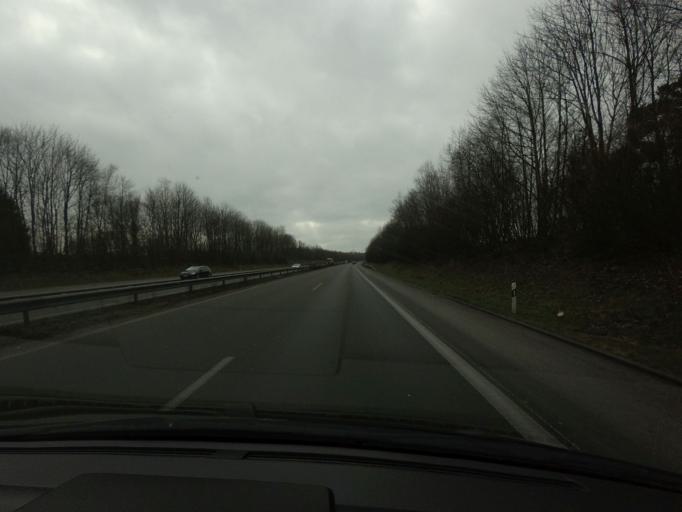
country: DE
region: Lower Saxony
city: Seevetal
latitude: 53.4129
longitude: 9.9209
